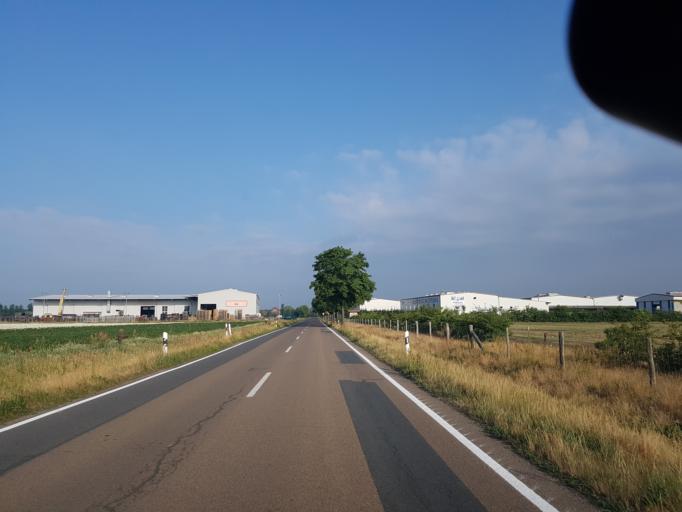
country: DE
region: Saxony-Anhalt
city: Holzdorf
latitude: 51.8527
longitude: 13.1126
